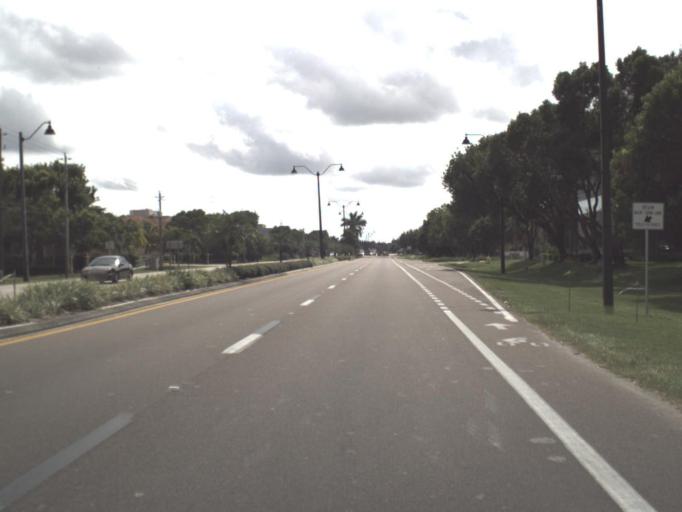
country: US
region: Florida
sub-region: Lee County
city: Fort Myers
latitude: 26.6044
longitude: -81.8507
